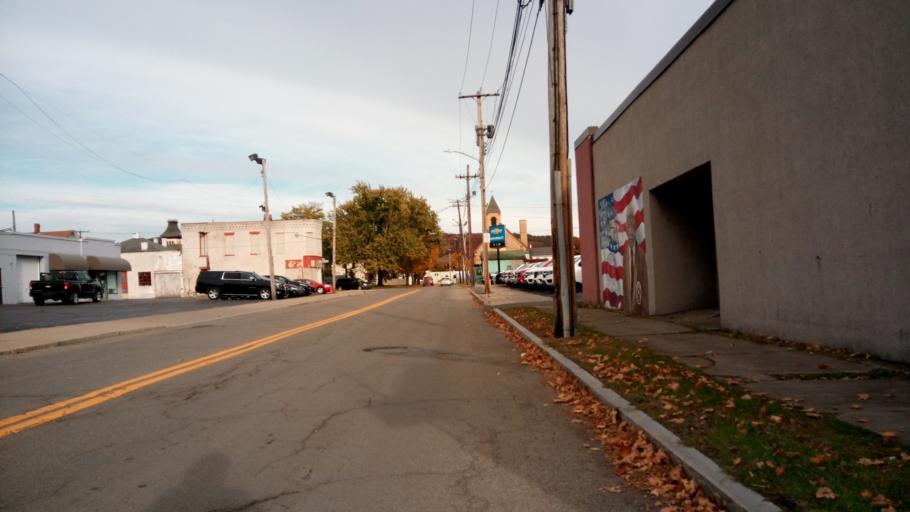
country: US
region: New York
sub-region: Chemung County
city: Elmira
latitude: 42.0924
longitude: -76.8058
